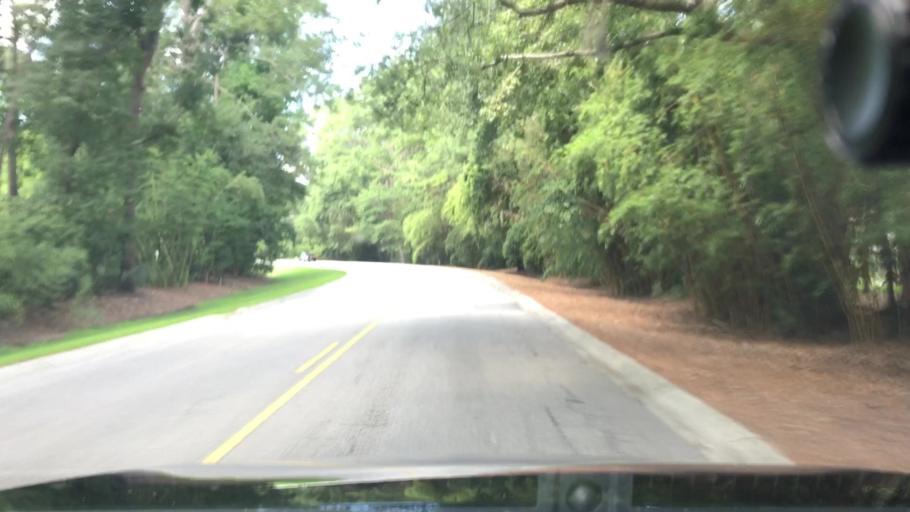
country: US
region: South Carolina
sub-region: Beaufort County
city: Hilton Head Island
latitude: 32.1494
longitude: -80.7787
